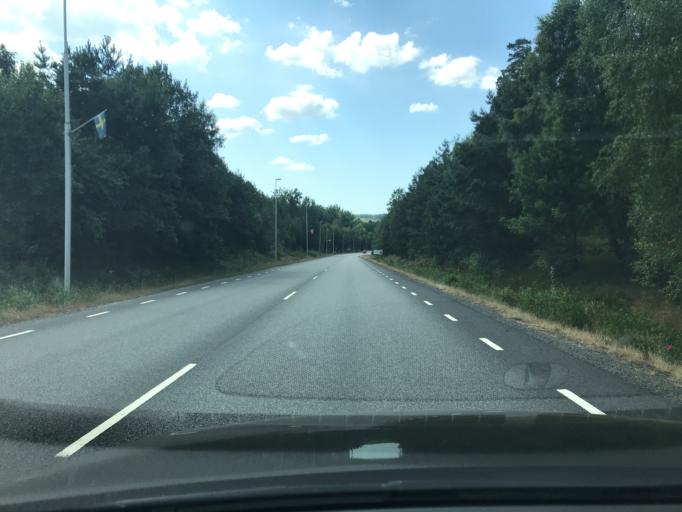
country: SE
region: Skane
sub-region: Hassleholms Kommun
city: Hastveda
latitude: 56.2762
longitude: 13.9433
